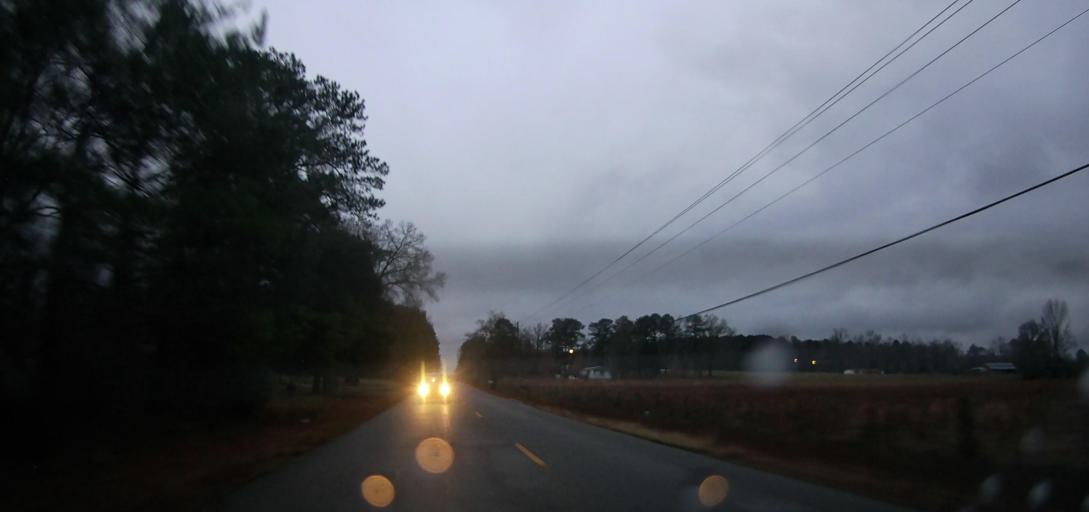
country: US
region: Alabama
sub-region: Tuscaloosa County
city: Vance
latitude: 33.1548
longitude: -87.2299
